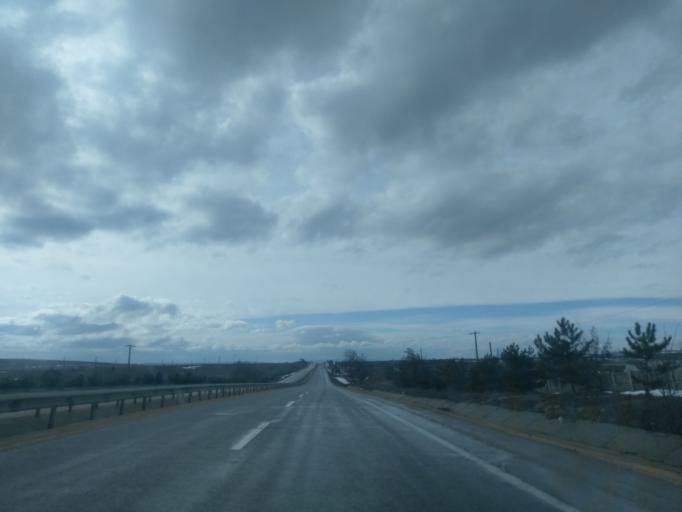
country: TR
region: Eskisehir
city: Inonu
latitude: 39.7228
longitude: 30.2546
